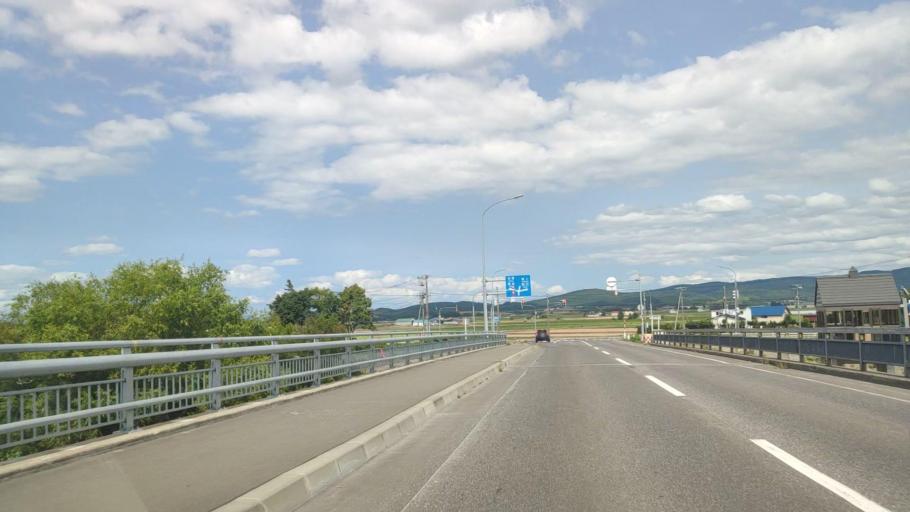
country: JP
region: Hokkaido
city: Nayoro
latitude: 44.1905
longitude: 142.4149
